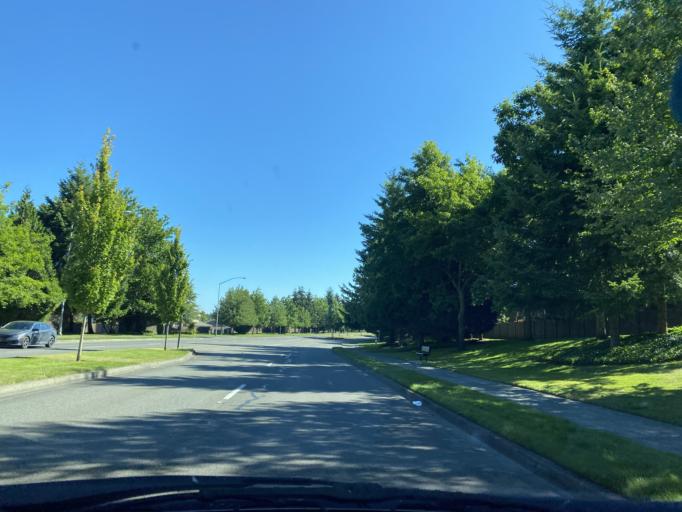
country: US
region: Washington
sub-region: Pierce County
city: McMillin
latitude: 47.1062
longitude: -122.2503
